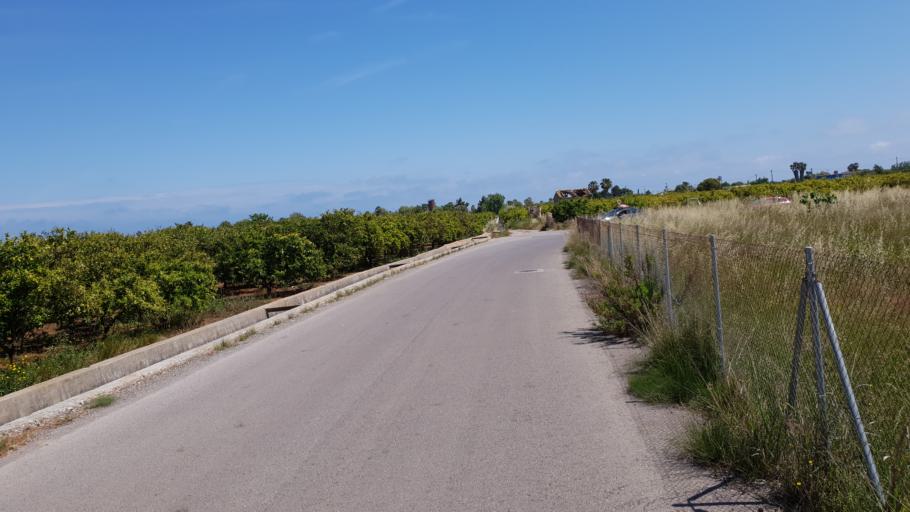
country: ES
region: Valencia
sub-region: Provincia de Castello
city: Burriana
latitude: 39.8621
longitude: -0.0891
